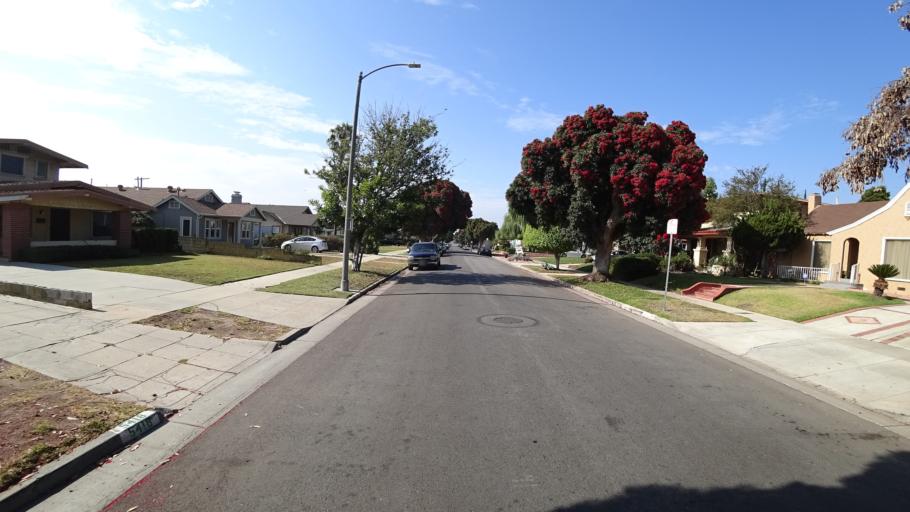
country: US
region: California
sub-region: Los Angeles County
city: View Park-Windsor Hills
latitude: 33.9924
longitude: -118.3345
